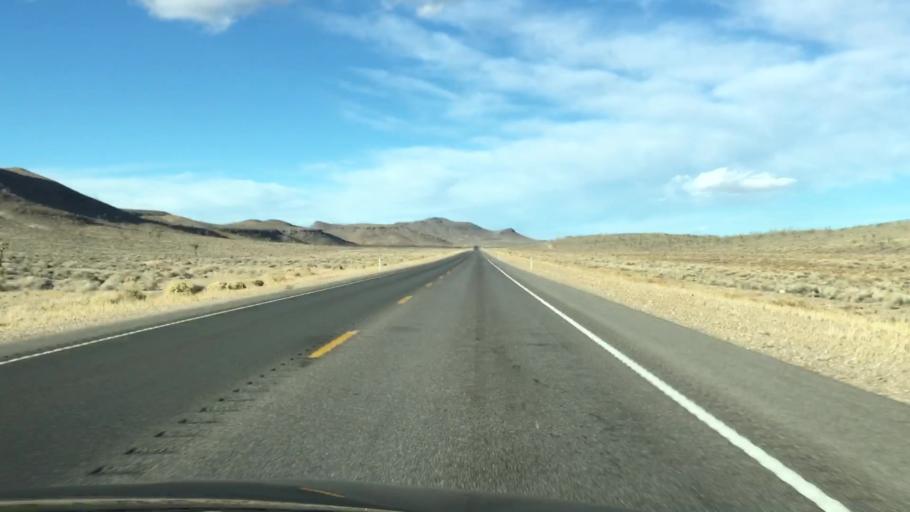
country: US
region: Nevada
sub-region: Esmeralda County
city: Goldfield
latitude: 37.6284
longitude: -117.2185
